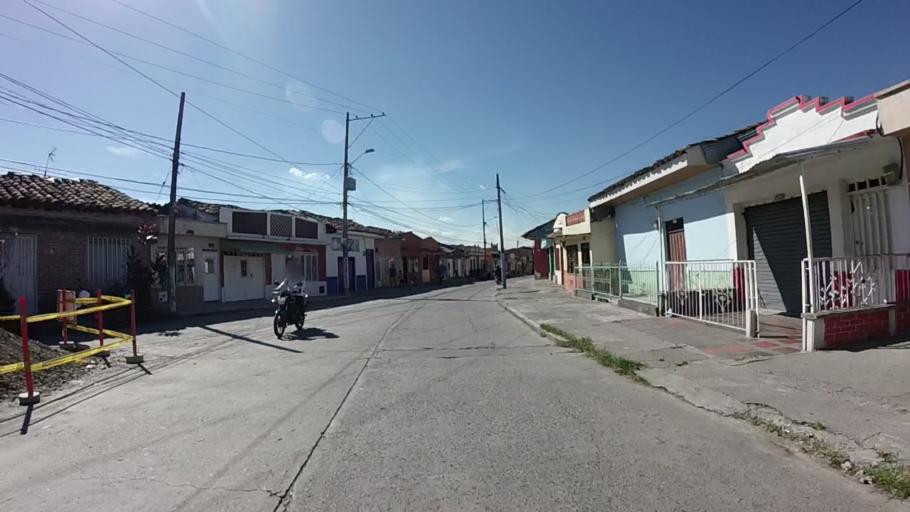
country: CO
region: Valle del Cauca
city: Cartago
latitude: 4.7414
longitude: -75.9080
